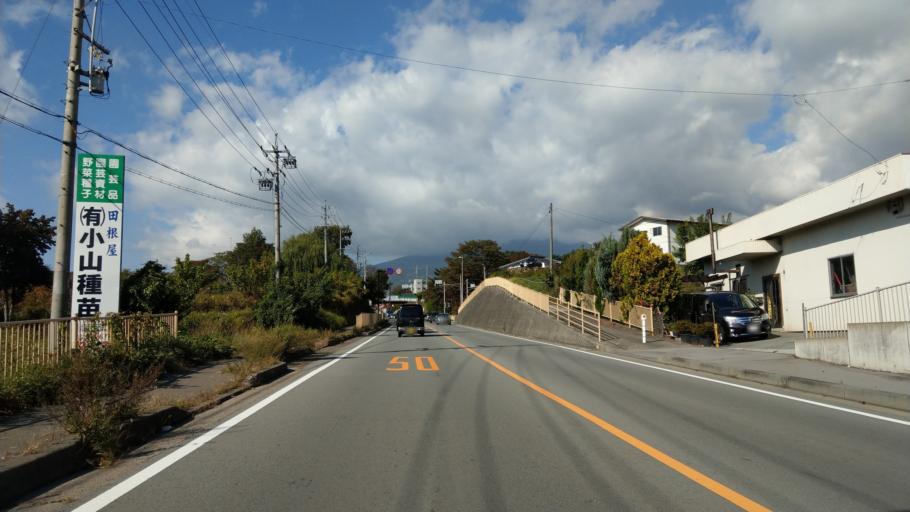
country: JP
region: Nagano
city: Komoro
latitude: 36.3225
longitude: 138.4365
